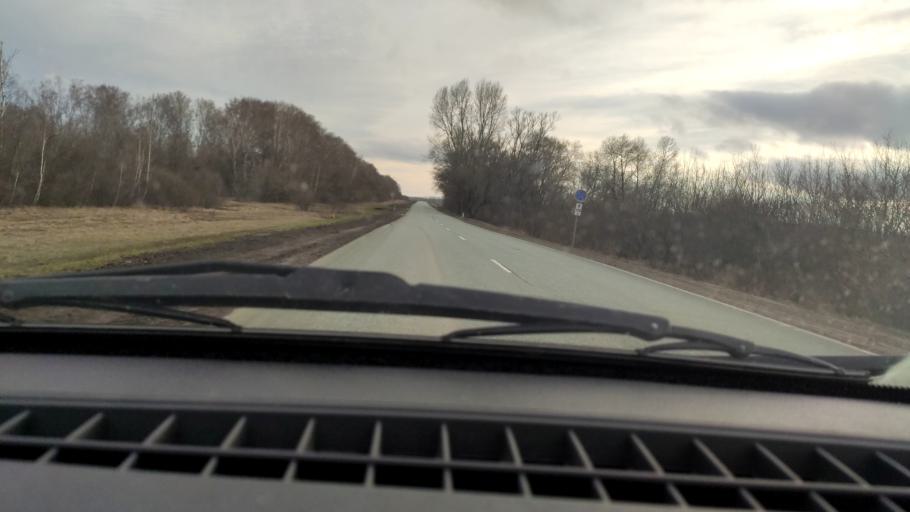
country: RU
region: Bashkortostan
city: Chishmy
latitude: 54.5355
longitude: 55.3121
